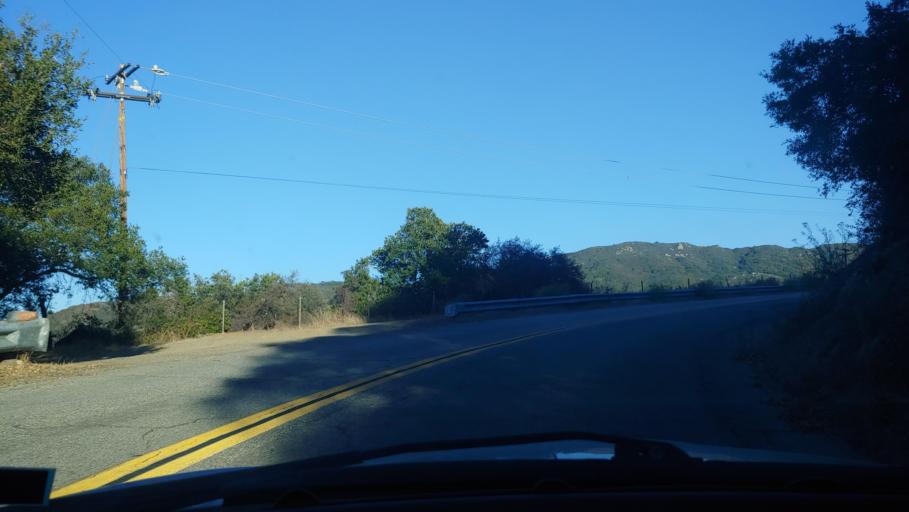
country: US
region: California
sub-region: Santa Barbara County
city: Goleta
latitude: 34.5240
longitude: -119.8334
